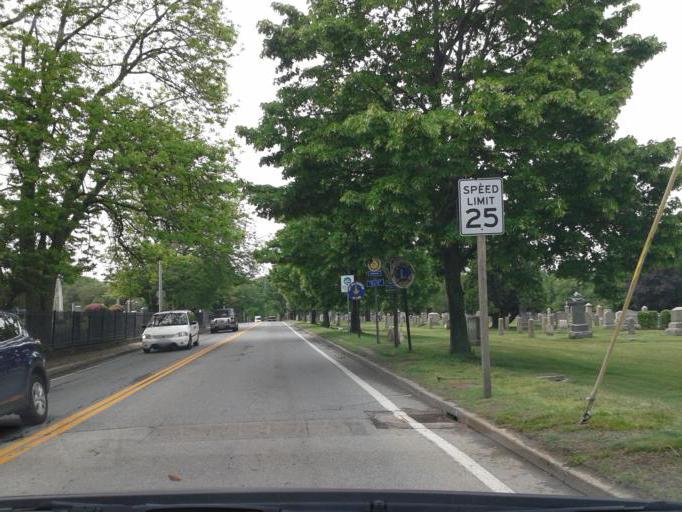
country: US
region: Rhode Island
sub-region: Newport County
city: Newport
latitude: 41.4986
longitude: -71.3171
